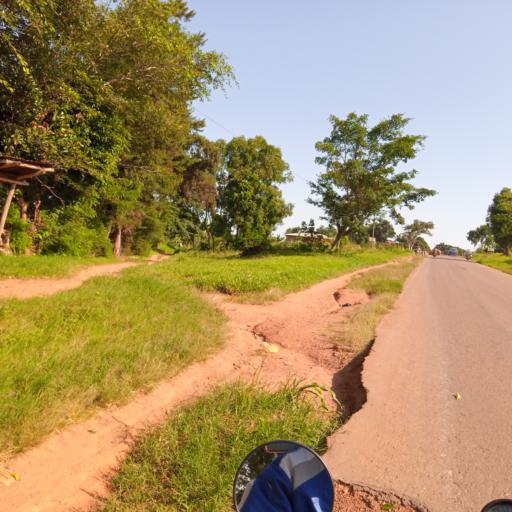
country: UG
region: Central Region
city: Masaka
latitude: -0.4392
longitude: 31.6636
